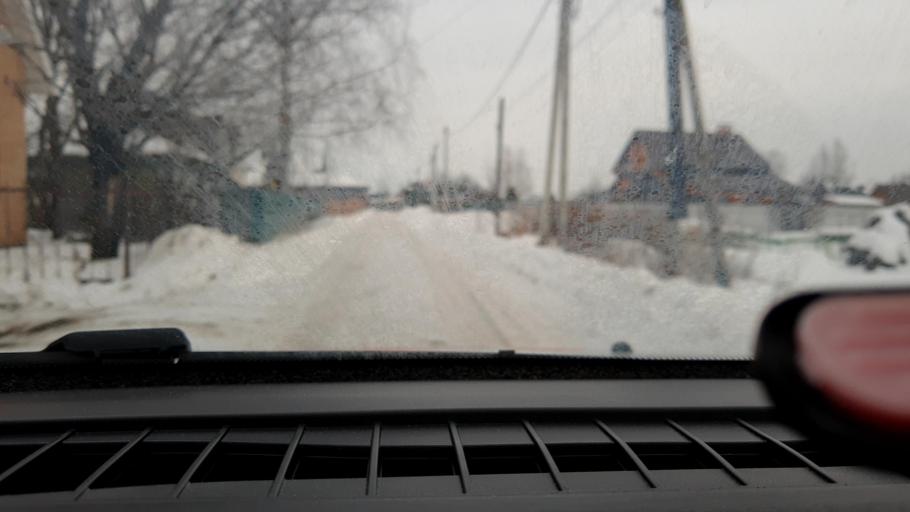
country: RU
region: Nizjnij Novgorod
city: Lukino
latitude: 56.4160
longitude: 43.6901
